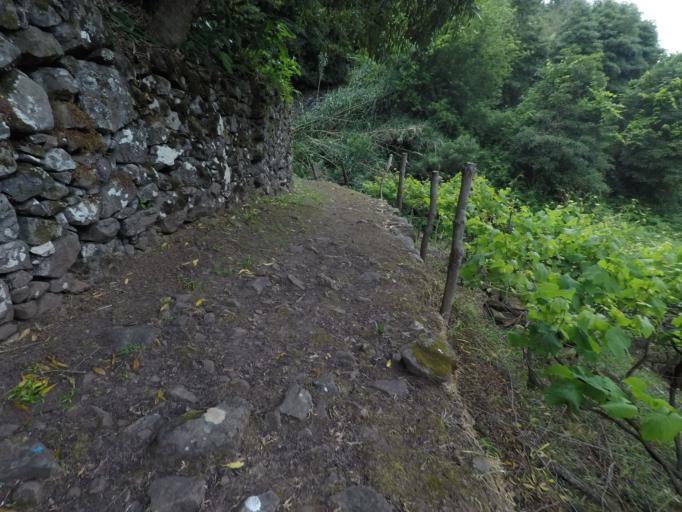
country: PT
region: Madeira
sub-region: Sao Vicente
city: Sao Vicente
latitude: 32.8168
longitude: -16.9681
